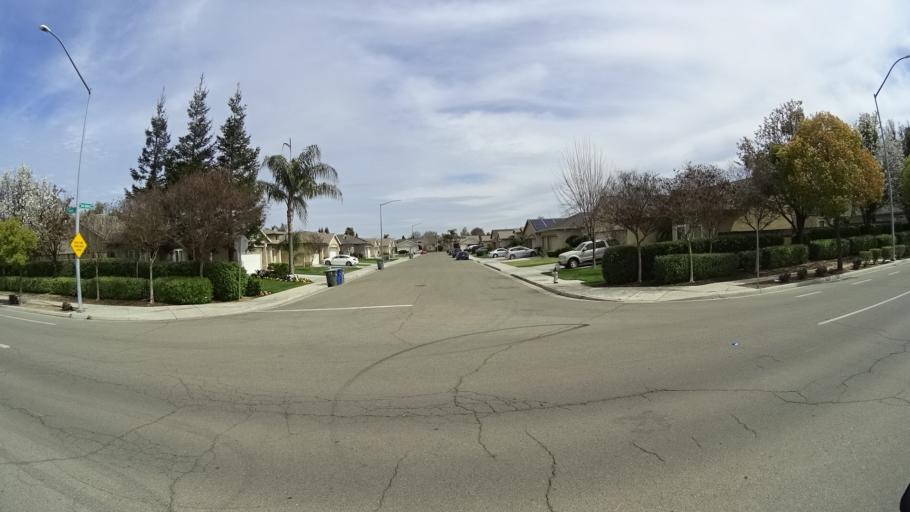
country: US
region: California
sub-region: Fresno County
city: West Park
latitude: 36.8030
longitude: -119.8985
